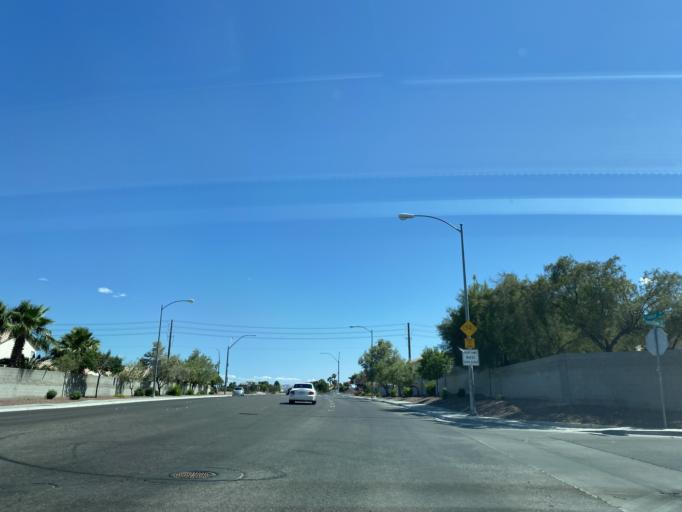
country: US
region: Nevada
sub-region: Clark County
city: Spring Valley
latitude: 36.0871
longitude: -115.2166
